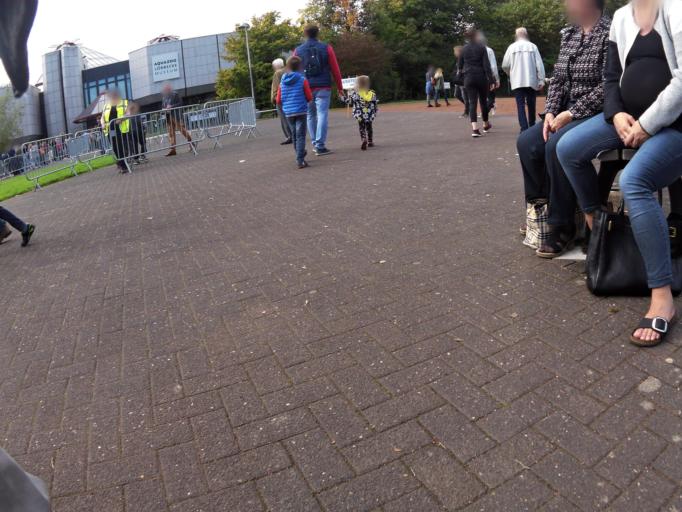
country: DE
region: North Rhine-Westphalia
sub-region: Regierungsbezirk Dusseldorf
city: Dusseldorf
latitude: 51.2567
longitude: 6.7508
